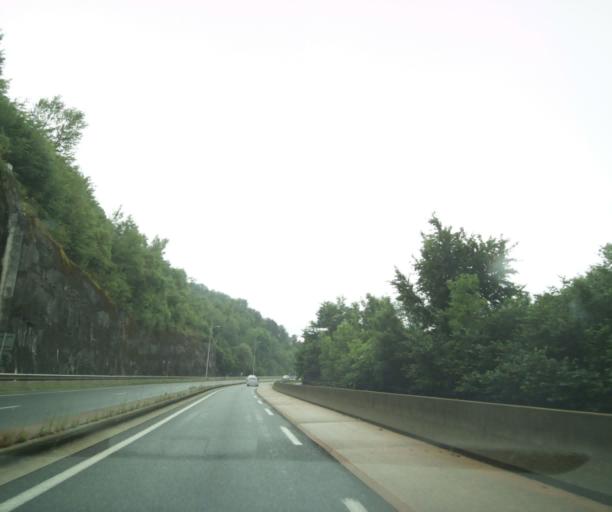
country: FR
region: Midi-Pyrenees
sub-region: Departement de l'Aveyron
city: Olemps
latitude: 44.3495
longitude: 2.5549
